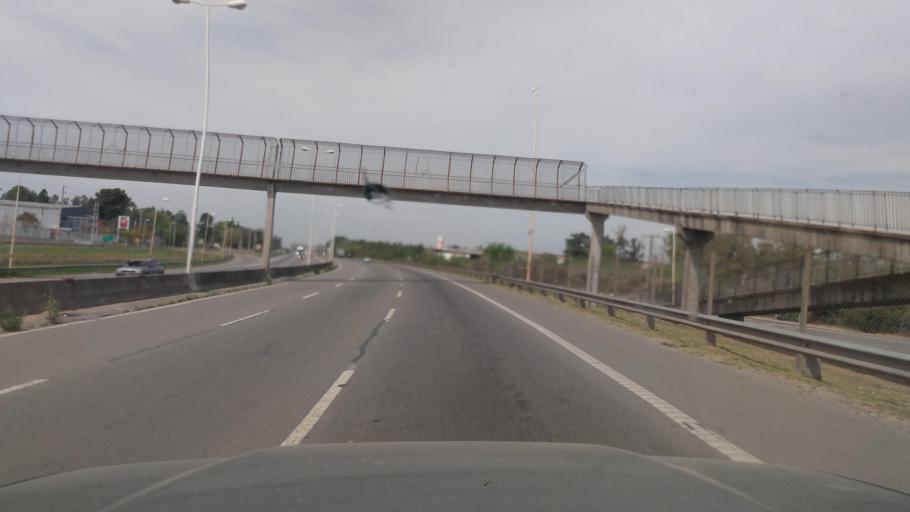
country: AR
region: Buenos Aires
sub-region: Partido de Pilar
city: Pilar
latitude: -34.4176
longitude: -59.0029
